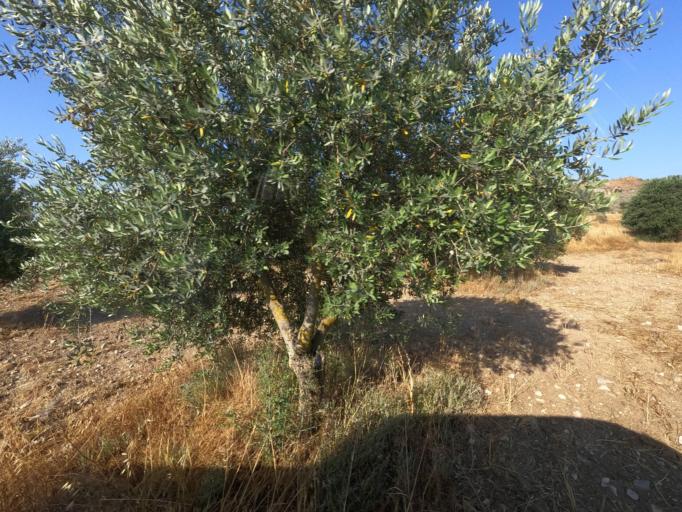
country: CY
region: Lefkosia
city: Lympia
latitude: 34.9955
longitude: 33.4329
